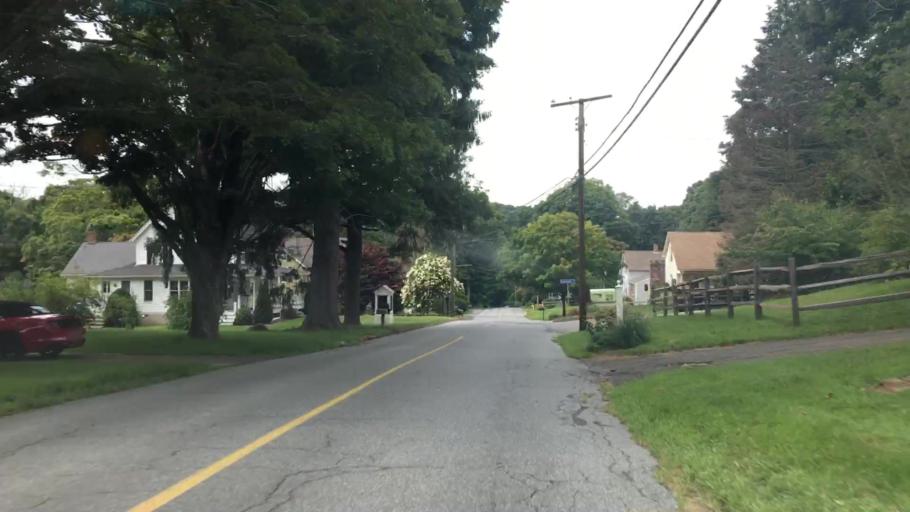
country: US
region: Connecticut
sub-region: Middlesex County
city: Deep River Center
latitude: 41.3430
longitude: -72.4456
